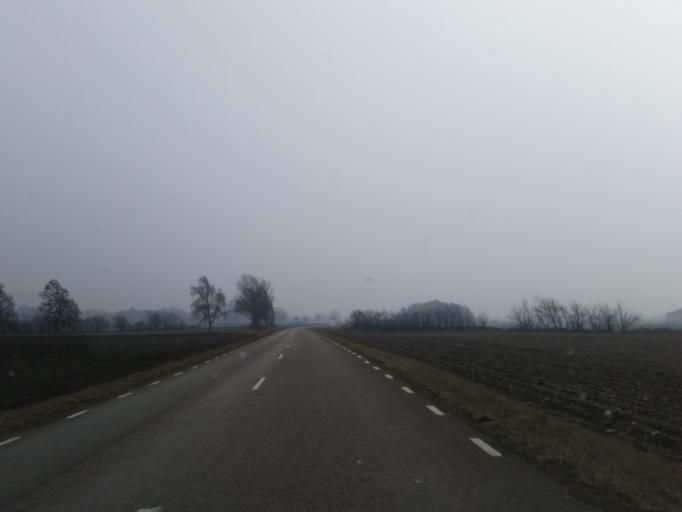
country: SE
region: Kalmar
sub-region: Morbylanga Kommun
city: Moerbylanga
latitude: 56.4126
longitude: 16.4137
